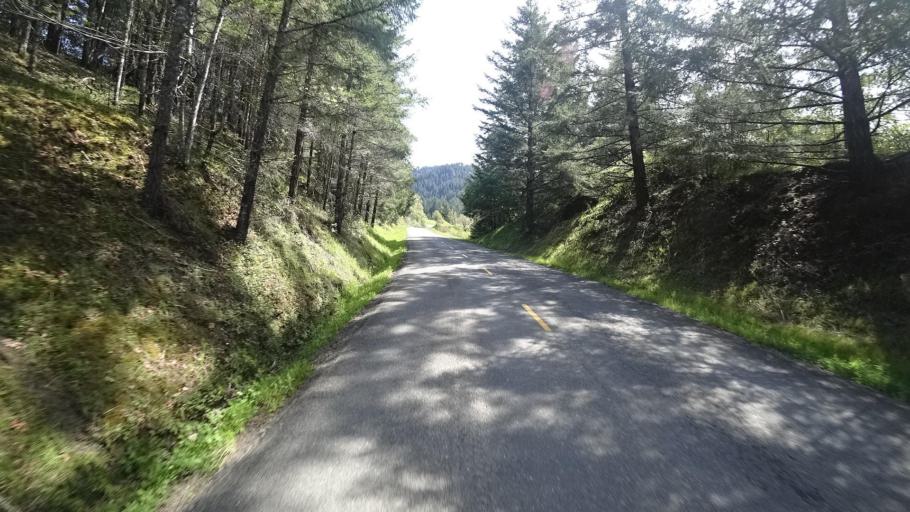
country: US
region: California
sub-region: Humboldt County
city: Rio Dell
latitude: 40.4640
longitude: -123.8043
